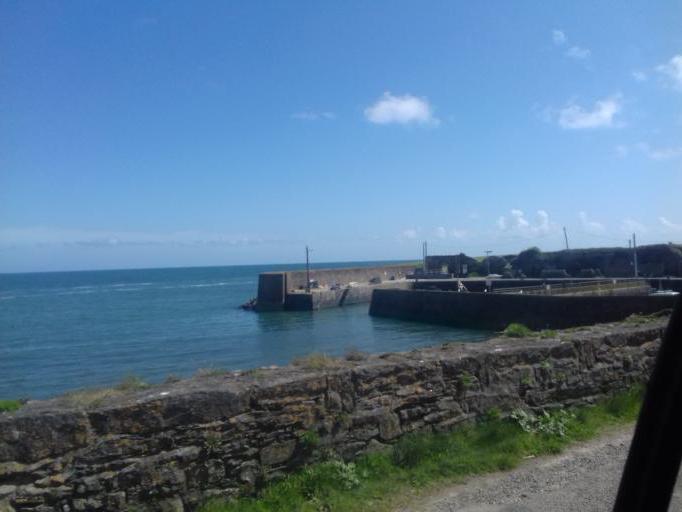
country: IE
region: Munster
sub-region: Waterford
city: Dunmore East
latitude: 52.1349
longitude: -6.9106
